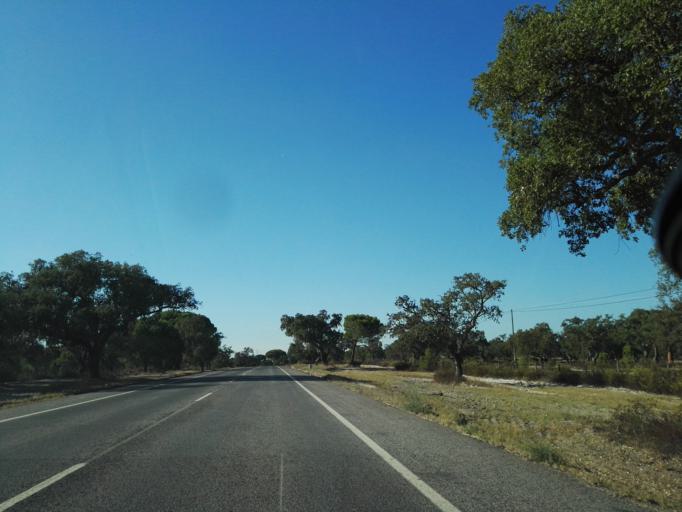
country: PT
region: Santarem
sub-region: Benavente
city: Poceirao
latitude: 38.8639
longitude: -8.7846
